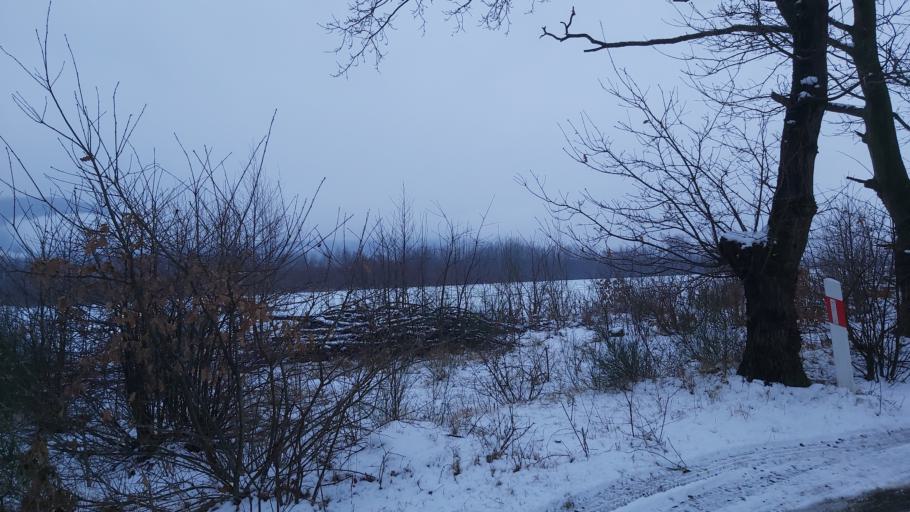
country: PL
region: Lower Silesian Voivodeship
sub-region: Powiat lubanski
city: Swieradow-Zdroj
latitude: 50.9475
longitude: 15.3450
